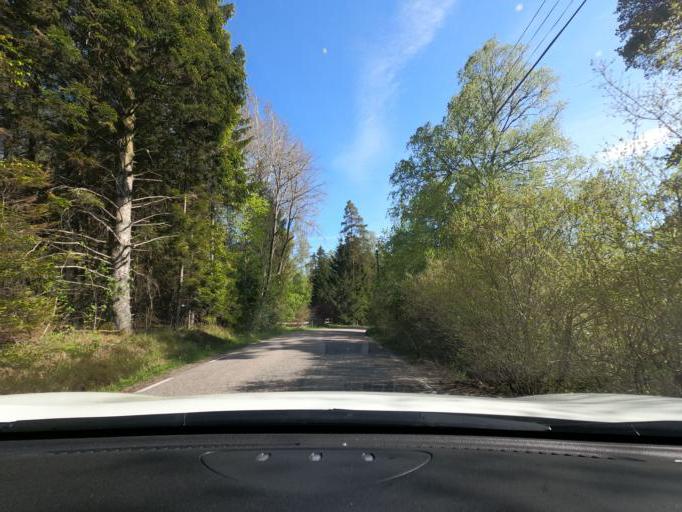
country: SE
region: Vaestra Goetaland
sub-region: Harryda Kommun
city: Hindas
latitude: 57.6709
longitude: 12.3516
